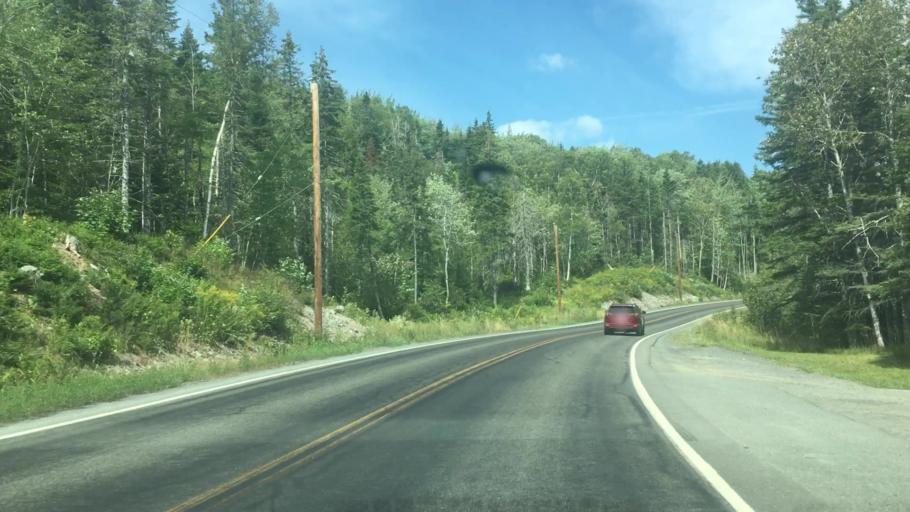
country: CA
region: Nova Scotia
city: Sydney Mines
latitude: 46.2067
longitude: -60.6226
